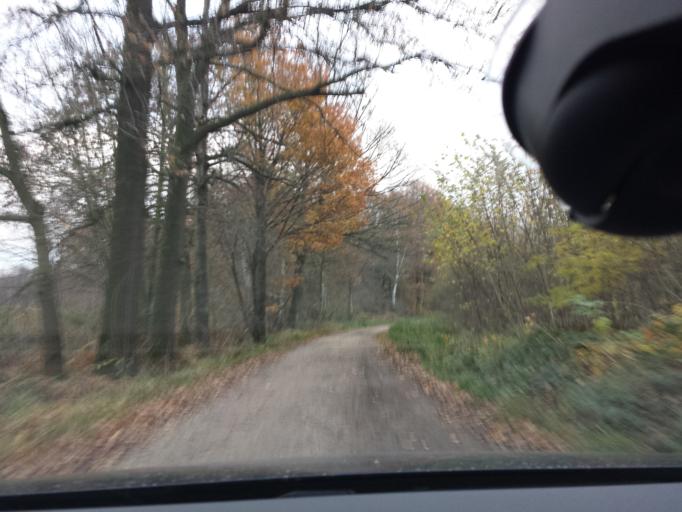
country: NL
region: Limburg
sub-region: Gemeente Heerlen
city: Heerlen
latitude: 50.9106
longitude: 6.0000
